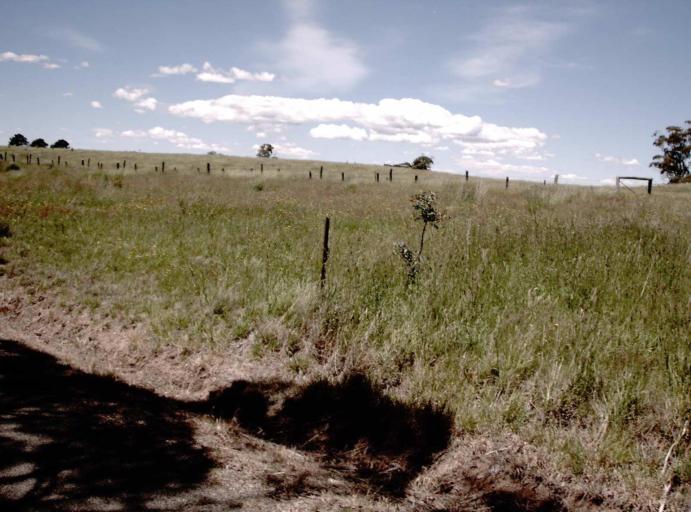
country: AU
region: New South Wales
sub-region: Snowy River
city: Jindabyne
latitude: -37.0853
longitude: 148.2736
